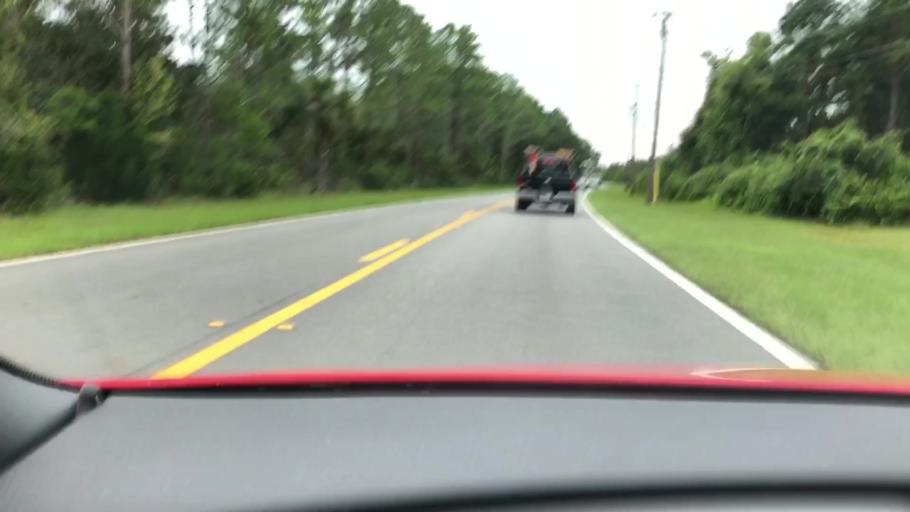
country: US
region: Florida
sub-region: Flagler County
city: Palm Coast
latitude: 29.5179
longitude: -81.1974
